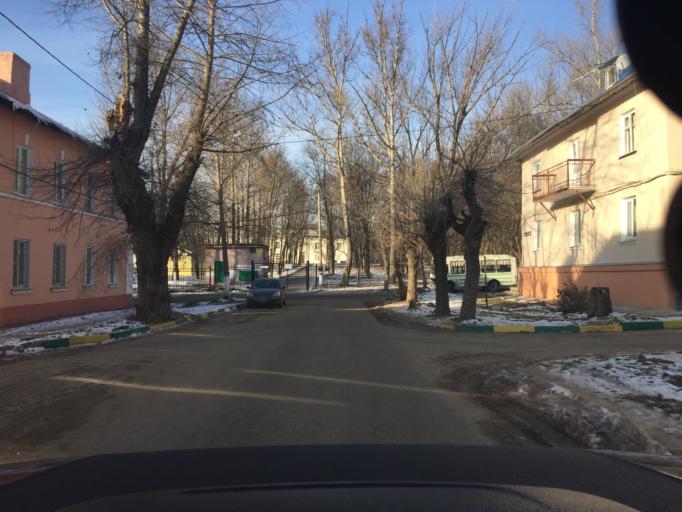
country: RU
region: Tula
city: Tula
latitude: 54.1834
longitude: 37.7032
